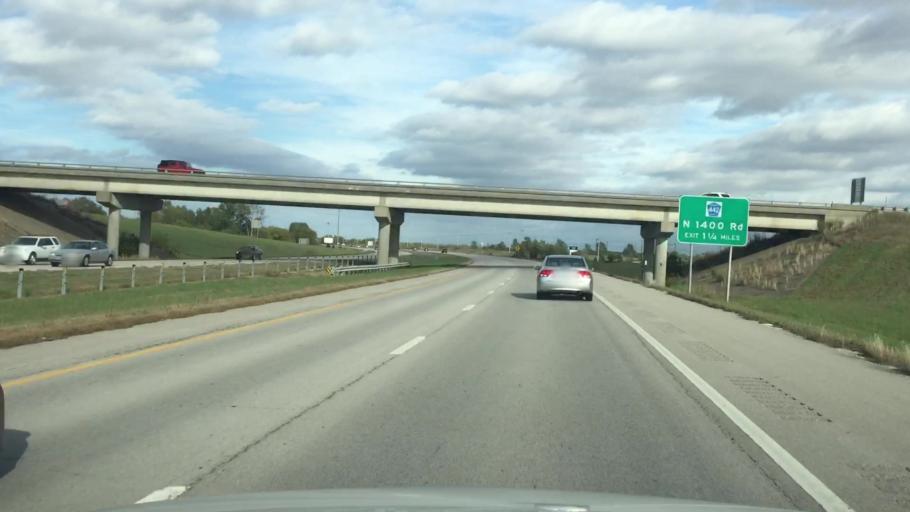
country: US
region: Kansas
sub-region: Douglas County
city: Eudora
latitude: 38.9308
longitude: -95.0979
